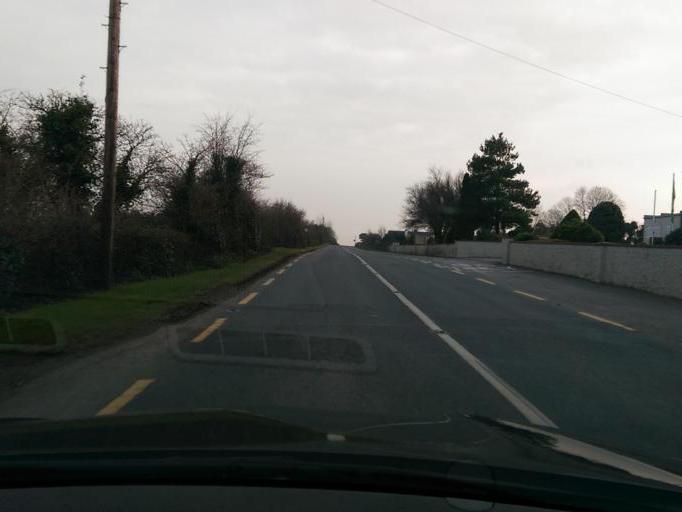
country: IE
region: Leinster
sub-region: An Iarmhi
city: Athlone
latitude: 53.4926
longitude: -7.8560
